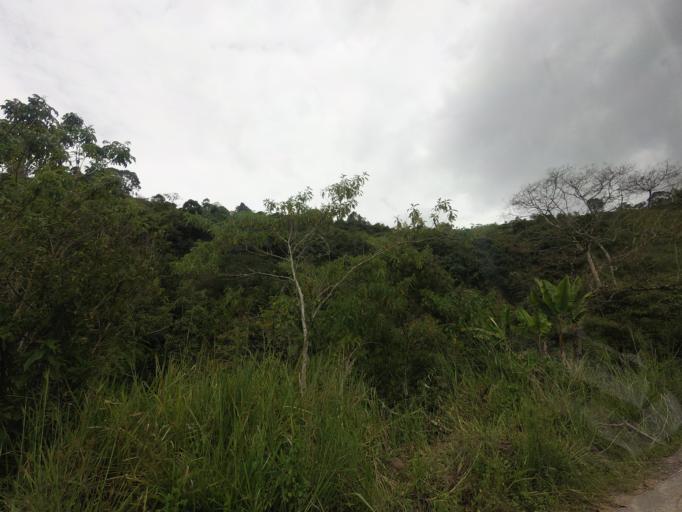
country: CO
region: Huila
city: San Agustin
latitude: 1.9293
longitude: -76.2996
